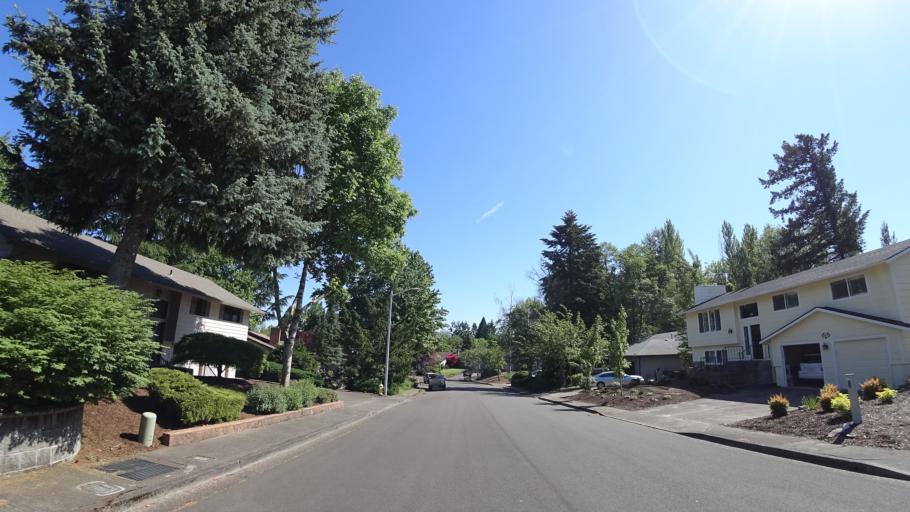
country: US
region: Oregon
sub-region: Washington County
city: Beaverton
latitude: 45.4595
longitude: -122.8050
